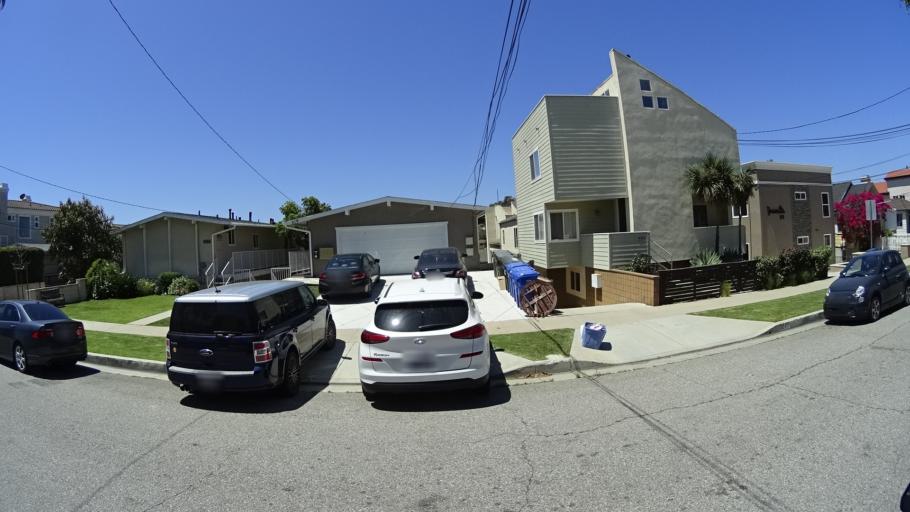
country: US
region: California
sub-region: Los Angeles County
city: Redondo Beach
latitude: 33.8442
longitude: -118.3798
